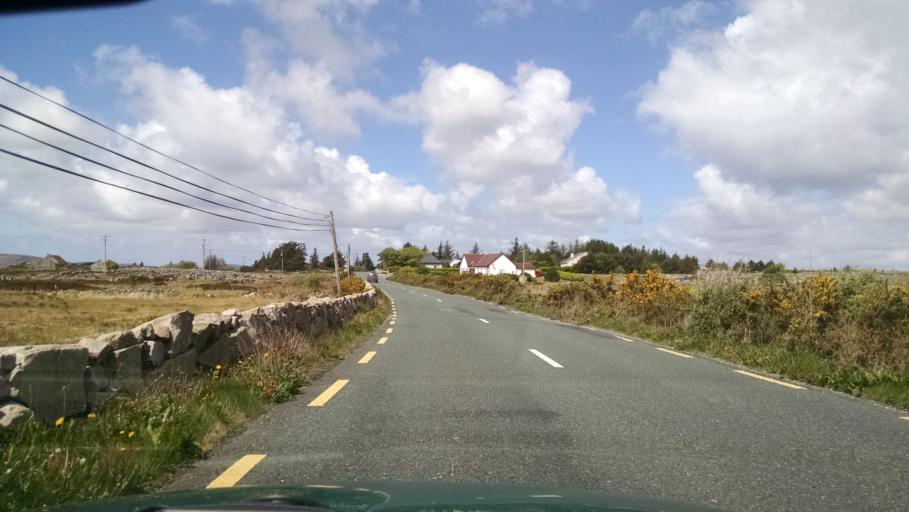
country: IE
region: Connaught
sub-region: County Galway
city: Oughterard
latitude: 53.3019
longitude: -9.5812
